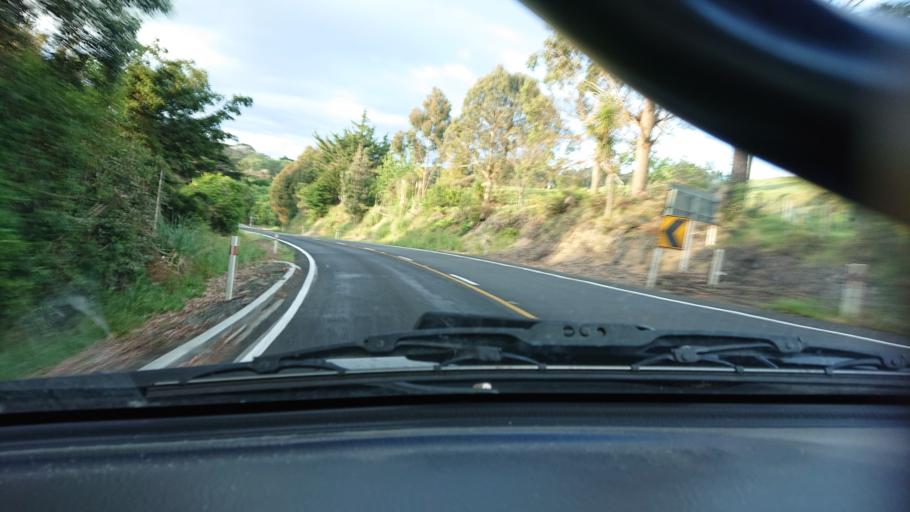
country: NZ
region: Auckland
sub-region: Auckland
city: Parakai
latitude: -36.5355
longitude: 174.4570
